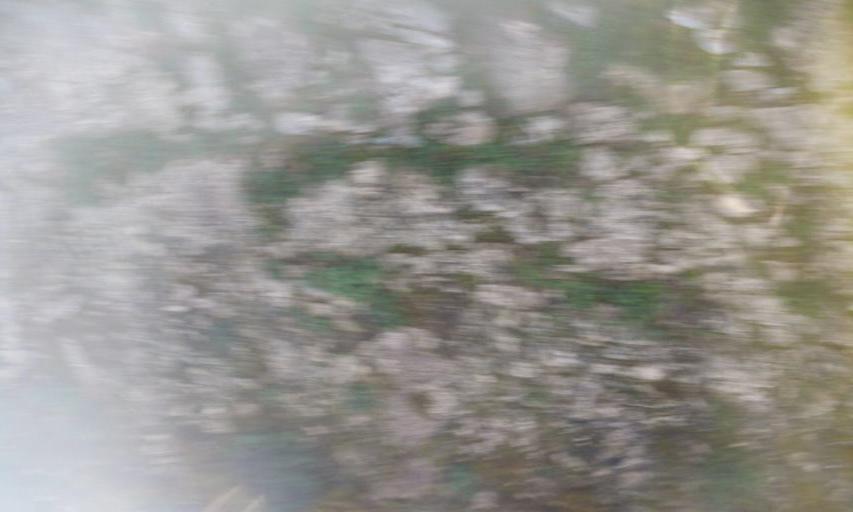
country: PT
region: Guarda
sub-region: Manteigas
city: Manteigas
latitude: 40.4906
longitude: -7.6032
